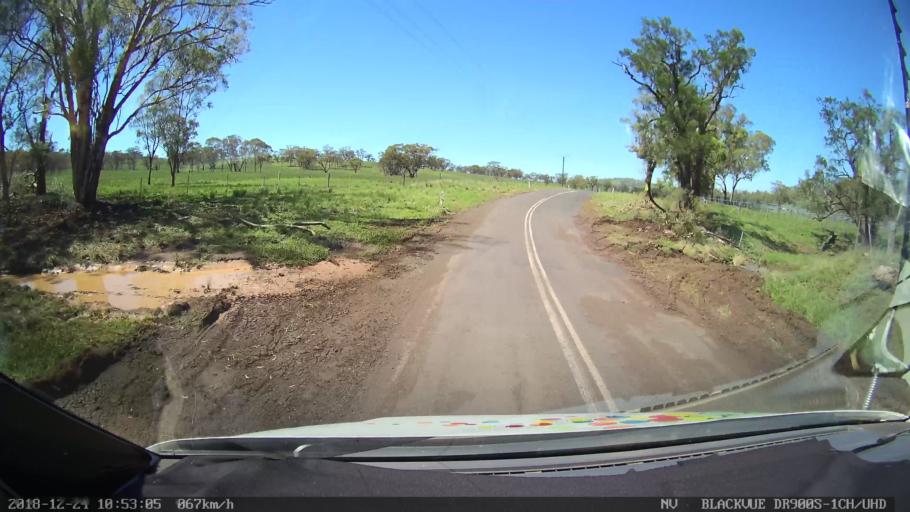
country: AU
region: New South Wales
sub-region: Upper Hunter Shire
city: Merriwa
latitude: -31.9881
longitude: 150.4229
